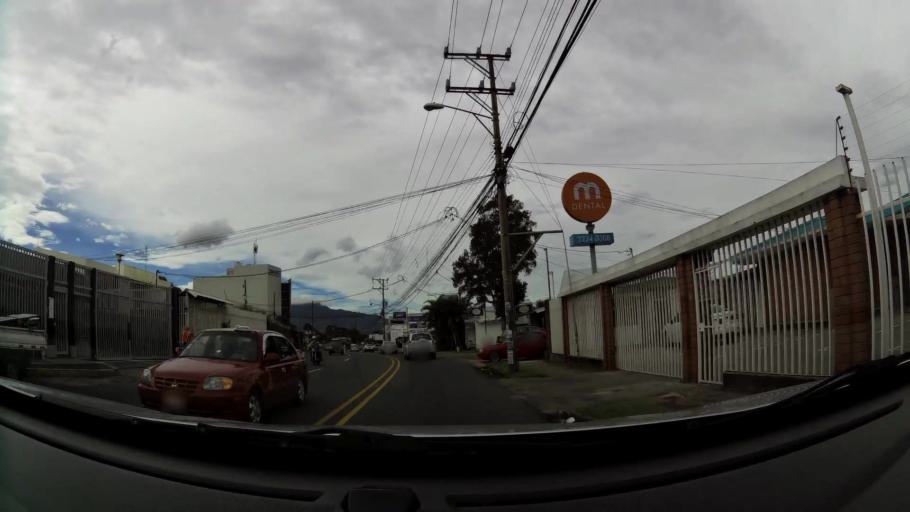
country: CR
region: San Jose
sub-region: Canton de Goicoechea
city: Guadalupe
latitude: 9.9405
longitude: -84.0509
